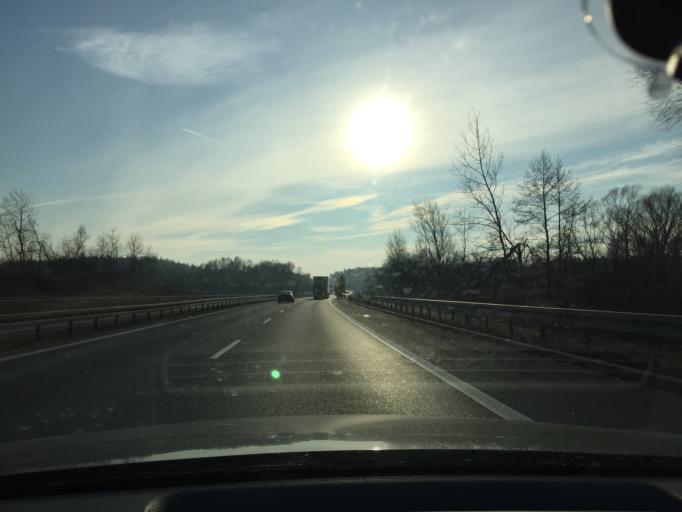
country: PL
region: Lesser Poland Voivodeship
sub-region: Powiat krakowski
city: Kryspinow
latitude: 50.0533
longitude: 19.8092
